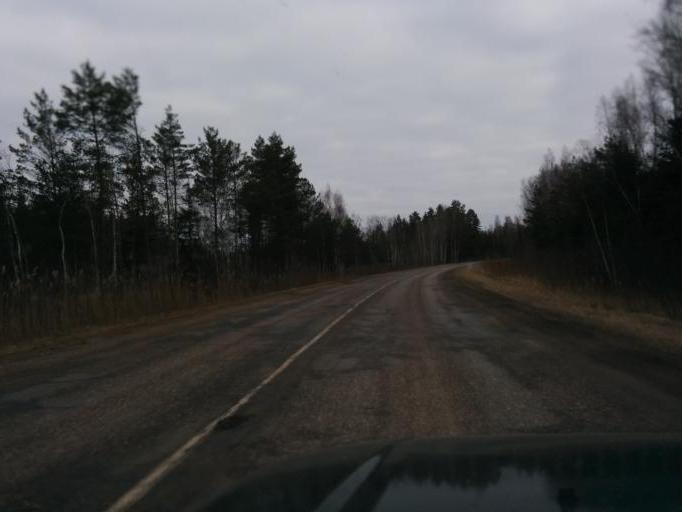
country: LV
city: Tireli
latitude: 56.8591
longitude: 23.5361
